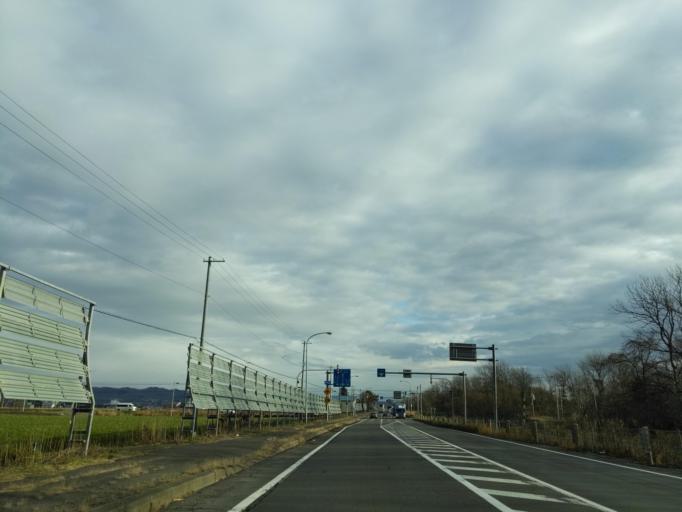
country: JP
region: Hokkaido
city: Kitahiroshima
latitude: 42.9677
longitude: 141.6695
